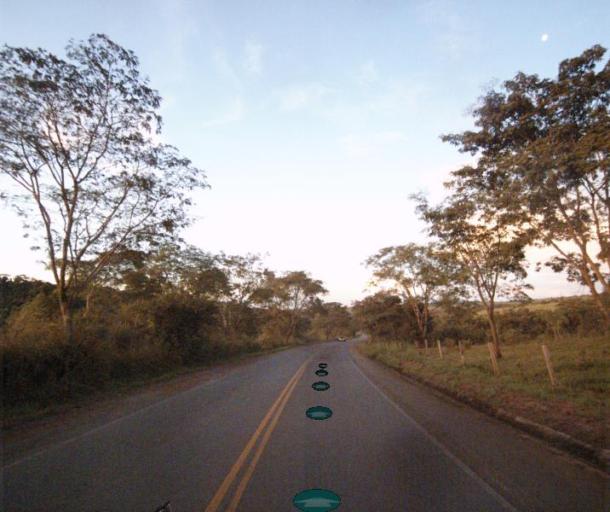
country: BR
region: Goias
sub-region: Pirenopolis
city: Pirenopolis
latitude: -15.9925
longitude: -48.8367
